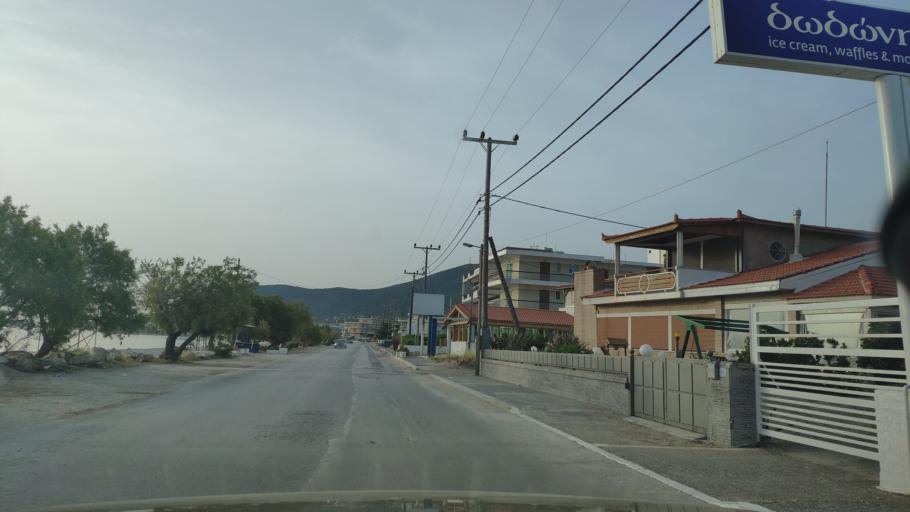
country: GR
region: Attica
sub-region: Nomarchia Anatolikis Attikis
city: Limin Mesoyaias
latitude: 37.8731
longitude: 24.0198
